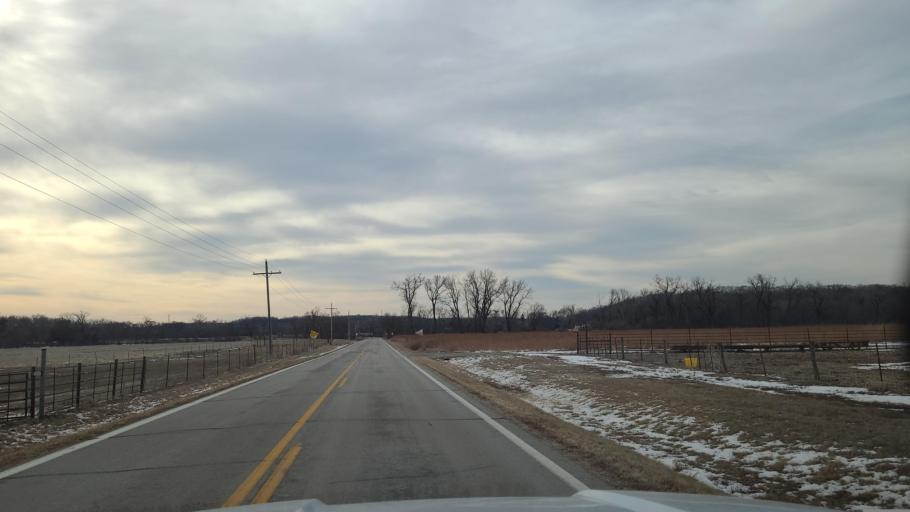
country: US
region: Kansas
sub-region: Douglas County
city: Lawrence
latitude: 39.0168
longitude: -95.2935
